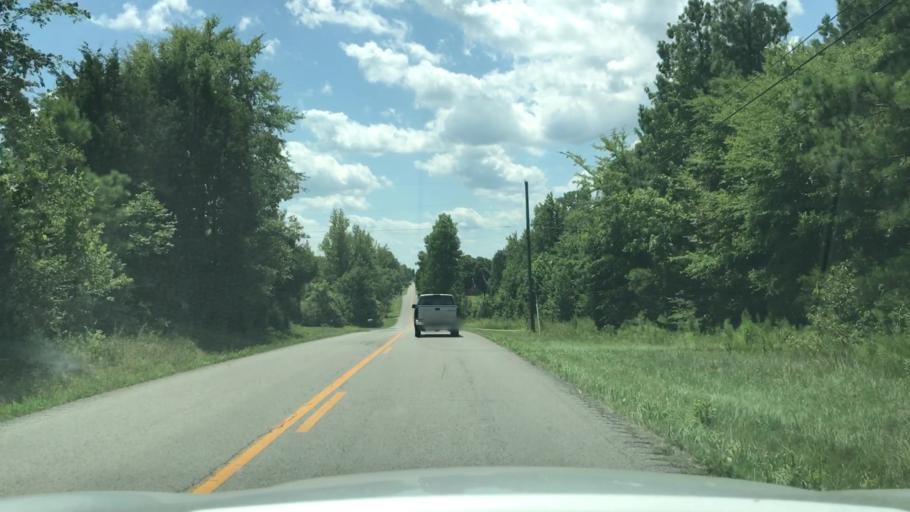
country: US
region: Kentucky
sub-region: Muhlenberg County
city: Greenville
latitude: 37.1764
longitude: -87.2403
